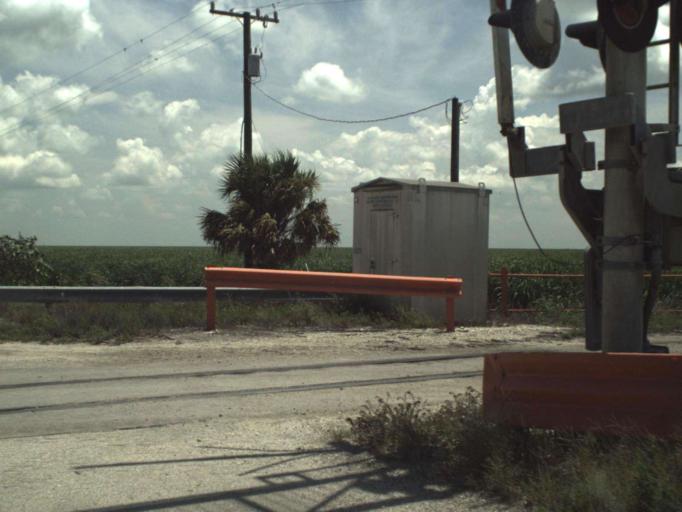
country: US
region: Florida
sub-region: Palm Beach County
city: Pahokee
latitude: 26.8470
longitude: -80.6084
